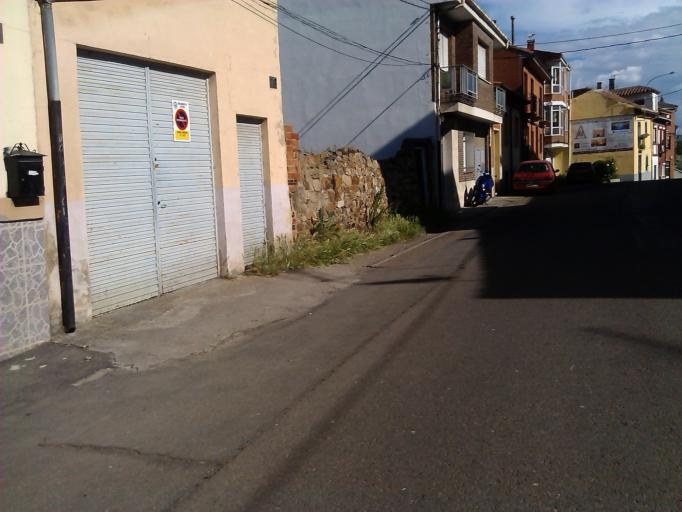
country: ES
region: Castille and Leon
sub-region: Provincia de Leon
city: Astorga
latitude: 42.4534
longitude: -6.0503
